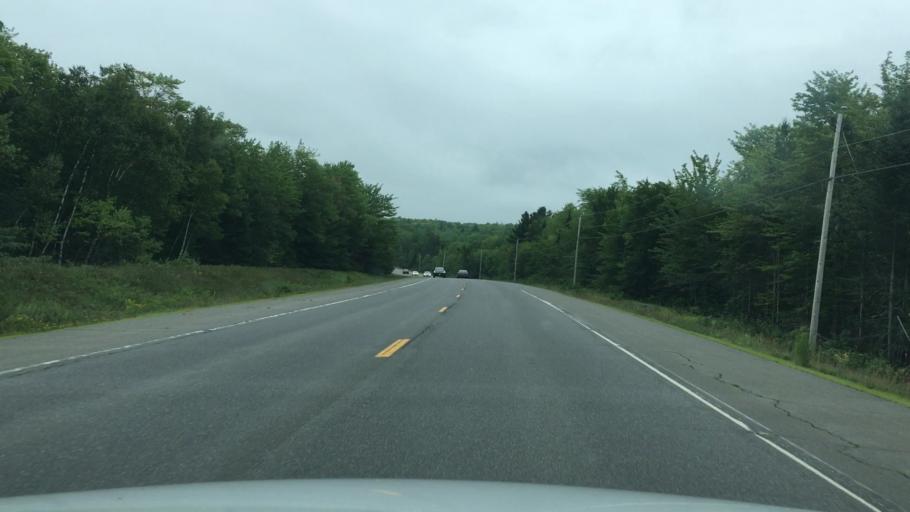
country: US
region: Maine
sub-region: Hancock County
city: Franklin
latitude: 44.8322
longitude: -68.1357
